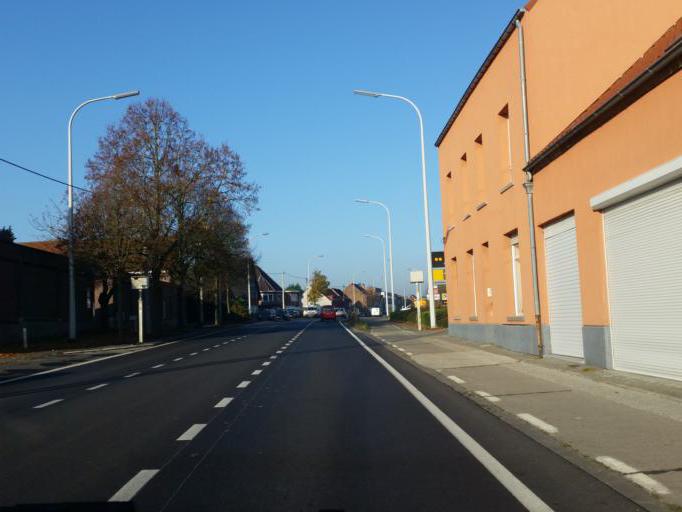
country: BE
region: Flanders
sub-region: Provincie Vlaams-Brabant
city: Asse
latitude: 50.9003
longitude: 4.2198
